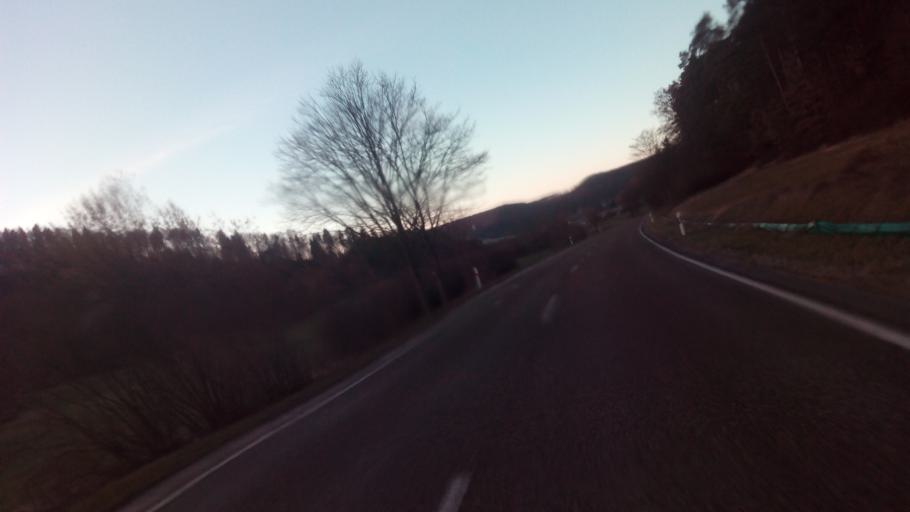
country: DE
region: Baden-Wuerttemberg
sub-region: Tuebingen Region
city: Schelklingen
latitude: 48.3583
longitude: 9.7459
